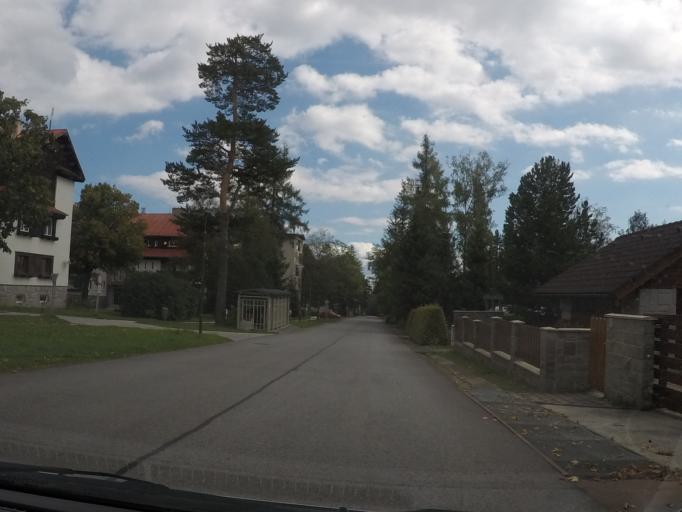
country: SK
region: Presovsky
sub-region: Okres Poprad
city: Nova Lesna
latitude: 49.1628
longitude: 20.2834
